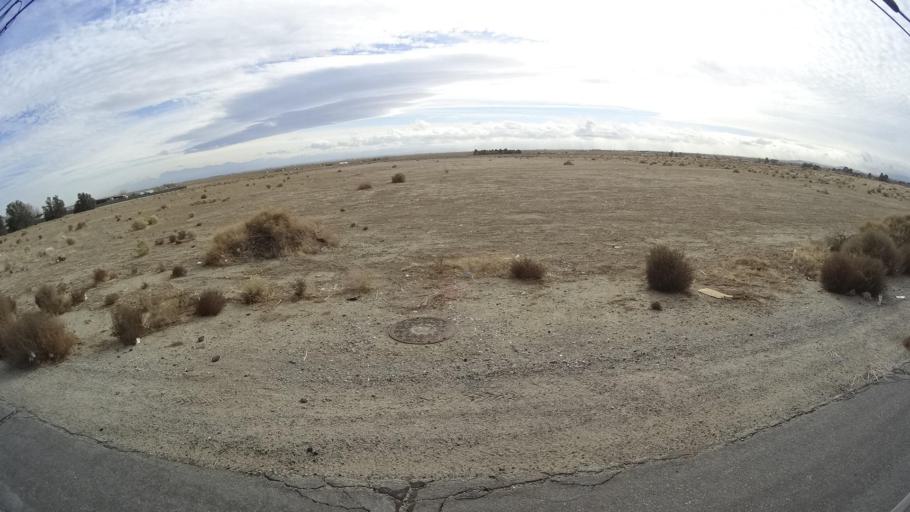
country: US
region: California
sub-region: Kern County
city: Rosamond
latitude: 34.8637
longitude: -118.2223
